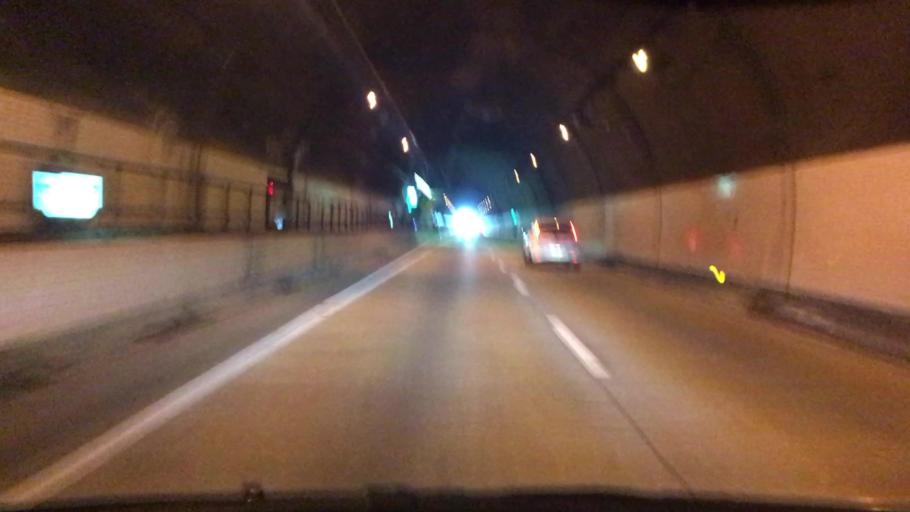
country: JP
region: Hyogo
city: Kobe
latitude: 34.7821
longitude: 135.2155
